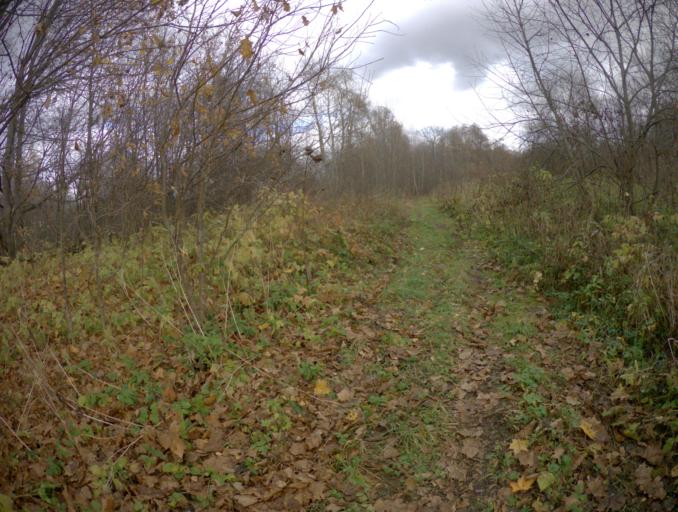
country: RU
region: Vladimir
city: Raduzhnyy
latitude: 56.0490
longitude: 40.3390
